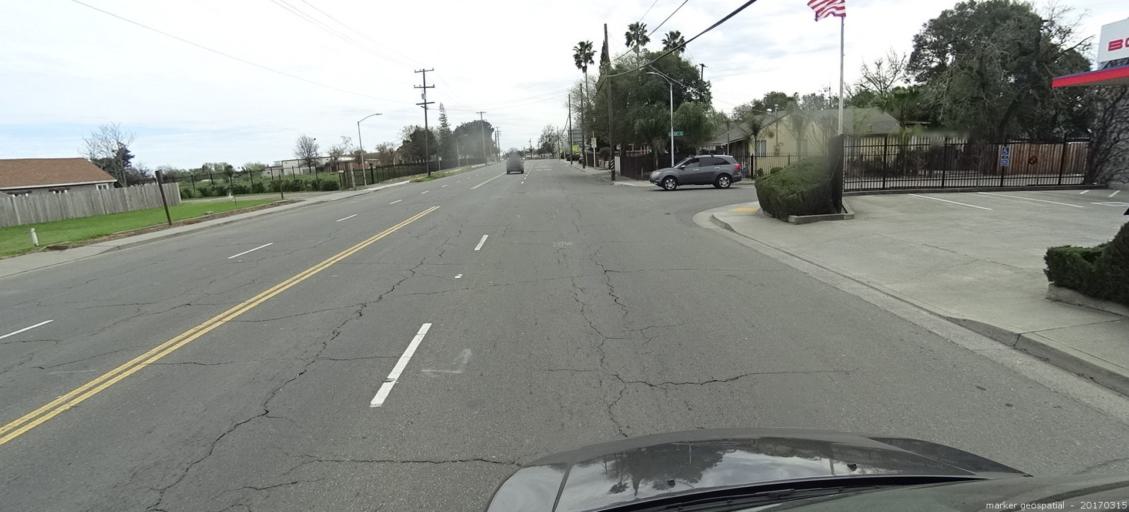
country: US
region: California
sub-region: Sacramento County
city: Parkway
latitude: 38.5220
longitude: -121.4711
